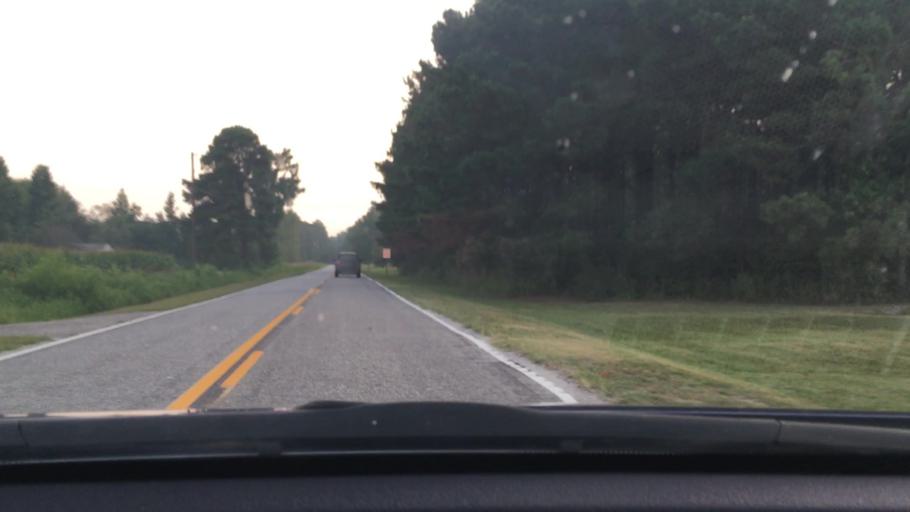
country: US
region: South Carolina
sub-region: Darlington County
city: Hartsville
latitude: 34.3268
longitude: -80.1045
